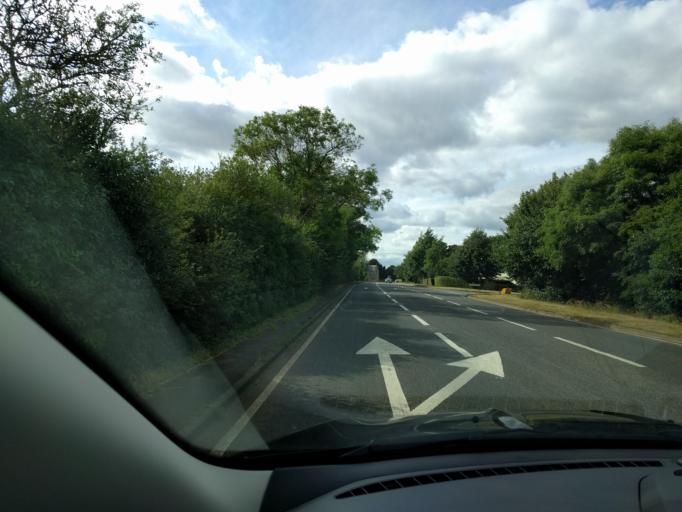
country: GB
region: England
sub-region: Warwickshire
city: Shipston on Stour
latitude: 52.1116
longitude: -1.6380
